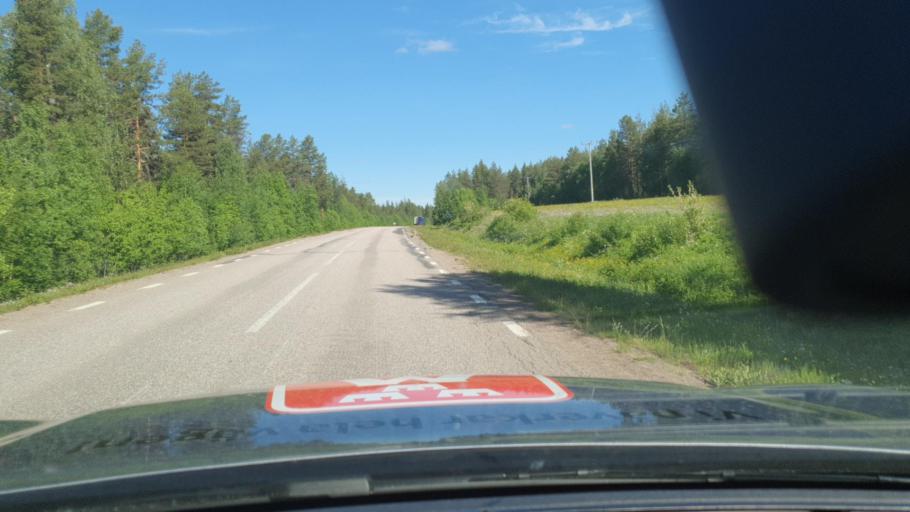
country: SE
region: Norrbotten
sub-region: Overkalix Kommun
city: OEverkalix
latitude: 66.6401
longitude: 22.7232
